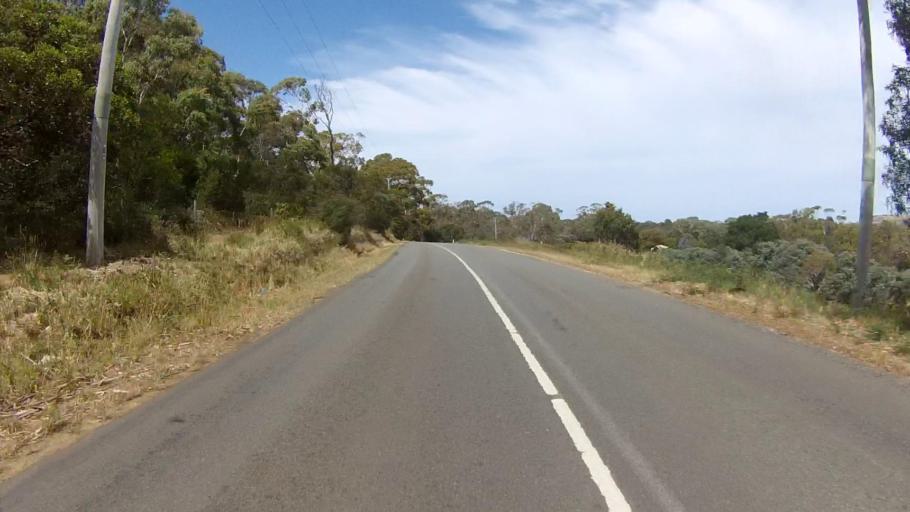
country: AU
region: Tasmania
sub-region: Kingborough
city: Taroona
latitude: -43.0169
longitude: 147.4172
